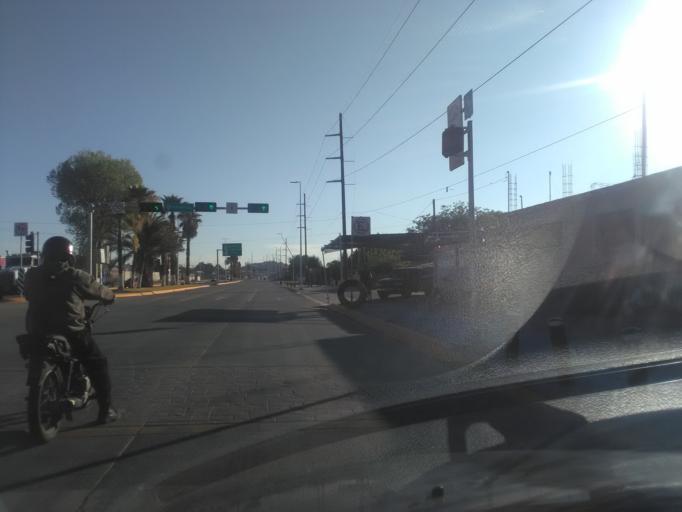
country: MX
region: Durango
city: Victoria de Durango
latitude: 23.9964
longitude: -104.7025
